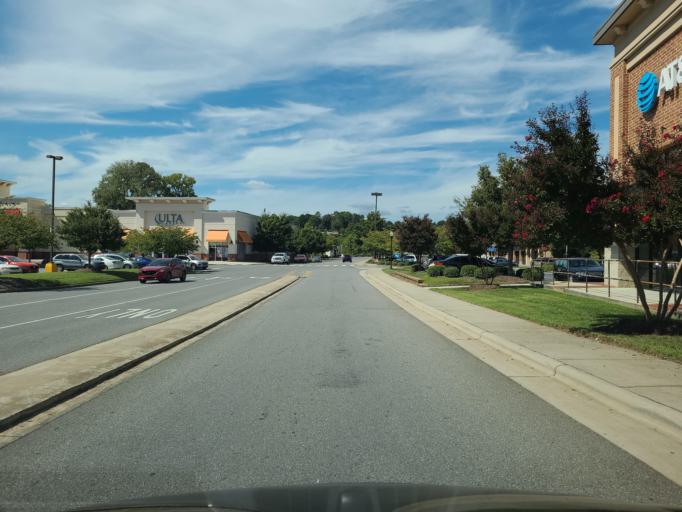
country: US
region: North Carolina
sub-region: Gaston County
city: Ranlo
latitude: 35.2631
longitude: -81.1341
